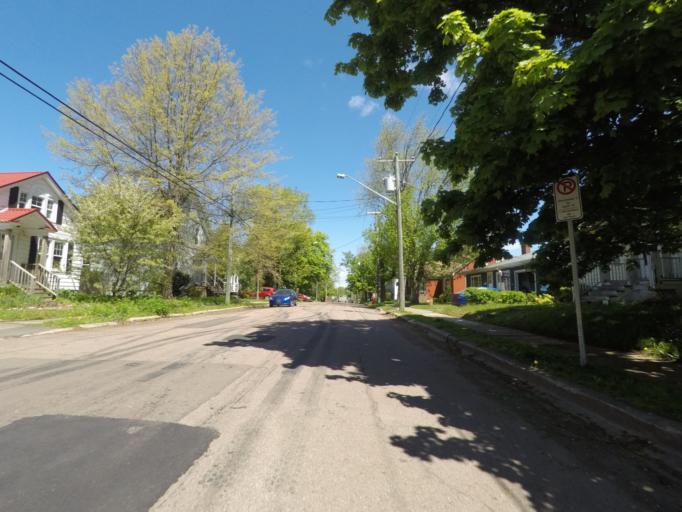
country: CA
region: New Brunswick
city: Moncton
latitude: 46.0983
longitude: -64.7925
